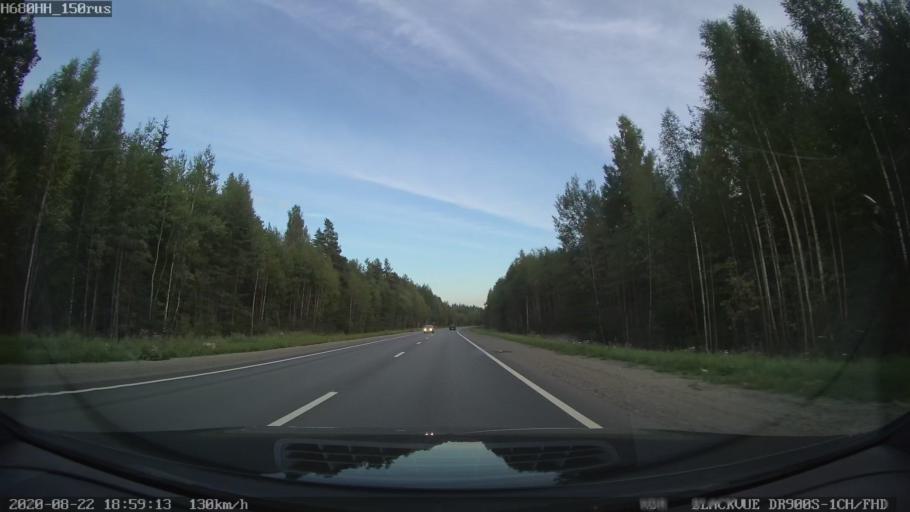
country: RU
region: Tverskaya
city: Rameshki
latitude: 57.1459
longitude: 36.0916
